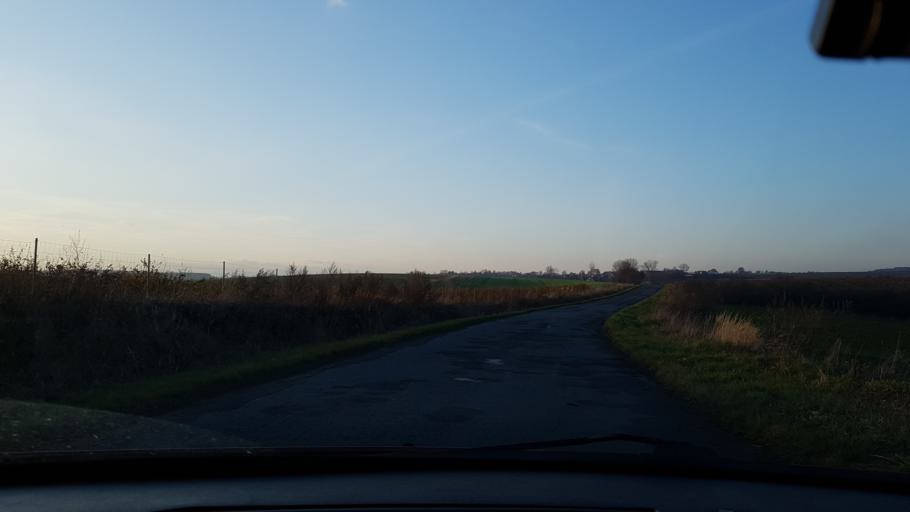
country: PL
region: Lower Silesian Voivodeship
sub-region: Powiat zabkowicki
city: Henrykow
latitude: 50.6592
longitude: 16.9974
